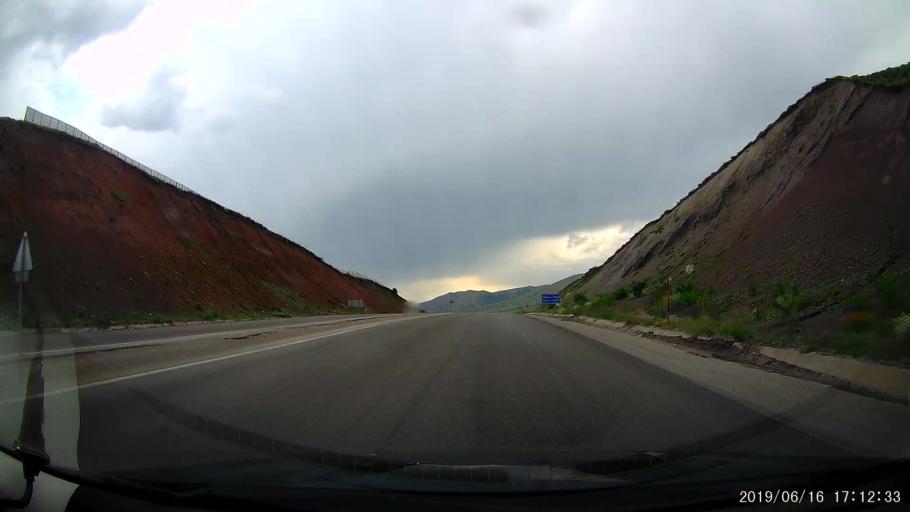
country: TR
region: Erzurum
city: Askale
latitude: 39.8593
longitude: 40.6167
